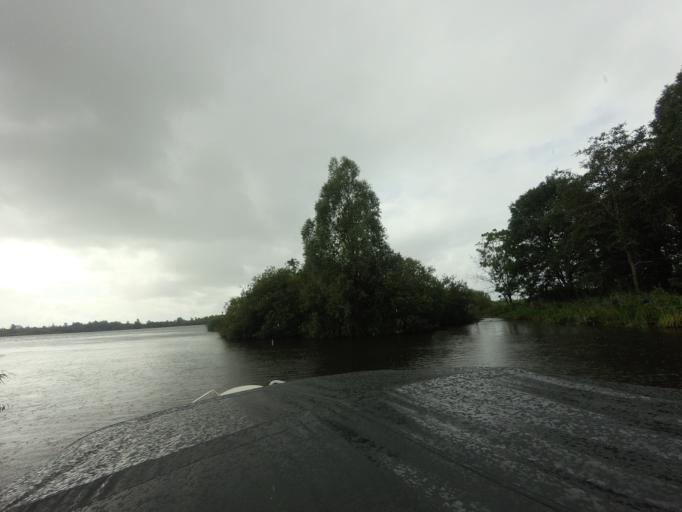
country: NL
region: Friesland
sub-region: Gemeente Boarnsterhim
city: Warten
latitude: 53.1366
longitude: 5.9080
